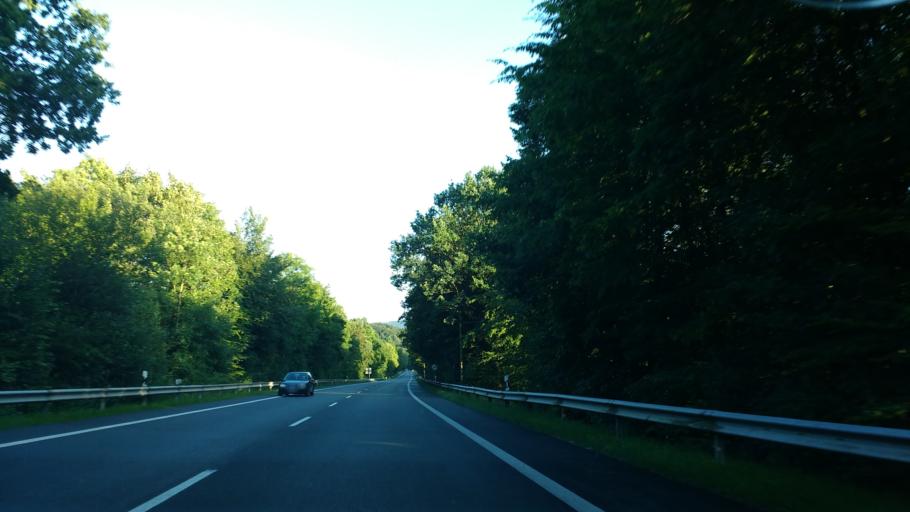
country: DE
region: North Rhine-Westphalia
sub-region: Regierungsbezirk Detmold
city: Barntrup
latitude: 52.0214
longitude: 9.1275
